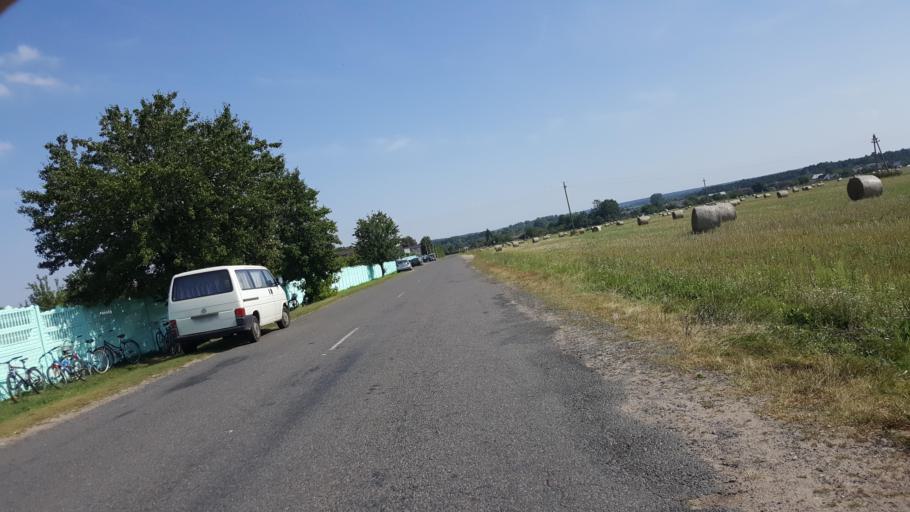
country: BY
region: Brest
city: Kamyanyets
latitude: 52.4105
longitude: 23.7913
